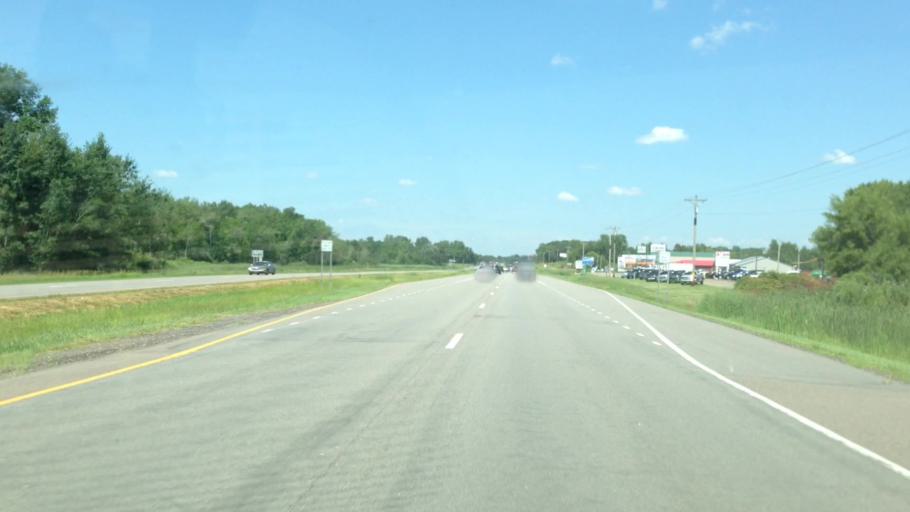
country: US
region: Minnesota
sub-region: Sherburne County
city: Zimmerman
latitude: 45.4275
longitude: -93.5723
